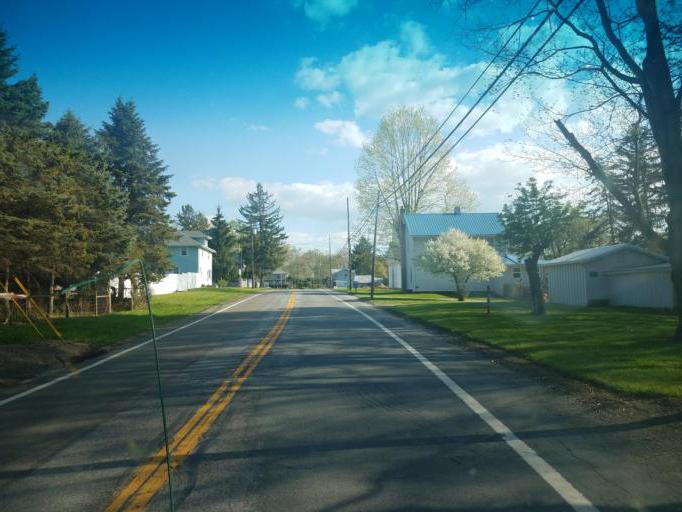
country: US
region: Ohio
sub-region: Wayne County
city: Shreve
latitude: 40.7134
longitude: -81.9451
